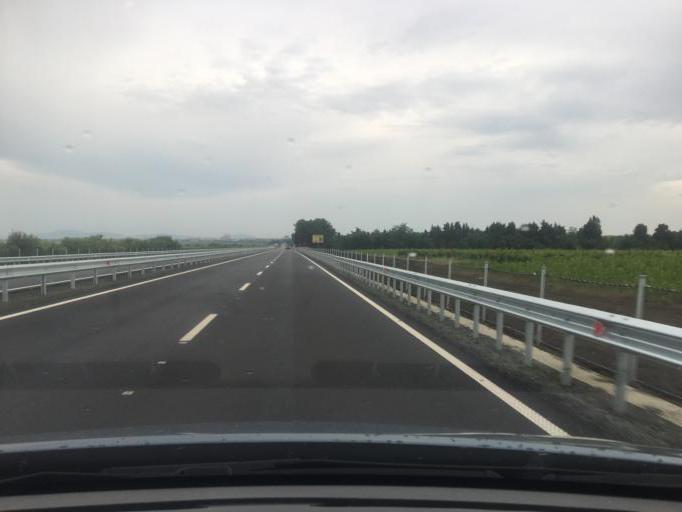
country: BG
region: Burgas
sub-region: Obshtina Pomorie
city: Pomorie
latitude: 42.6014
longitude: 27.6180
